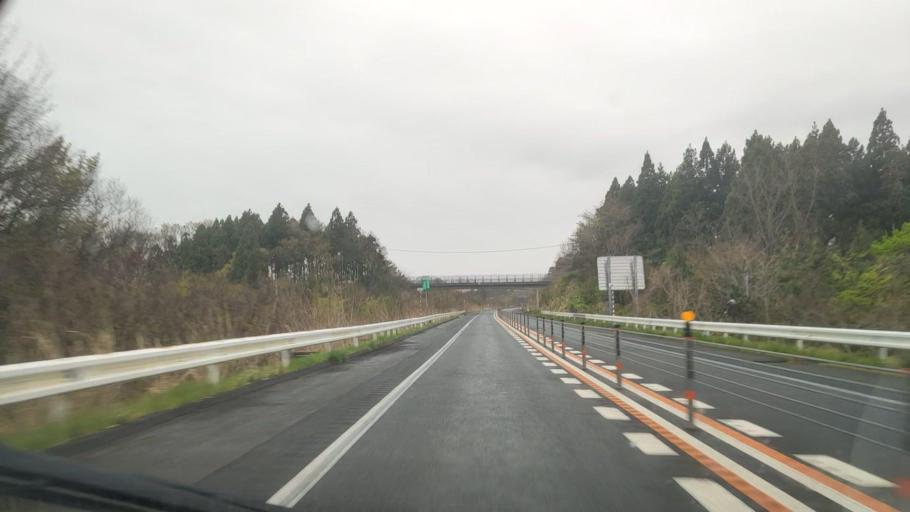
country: JP
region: Akita
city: Noshiromachi
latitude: 40.1470
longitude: 140.0205
